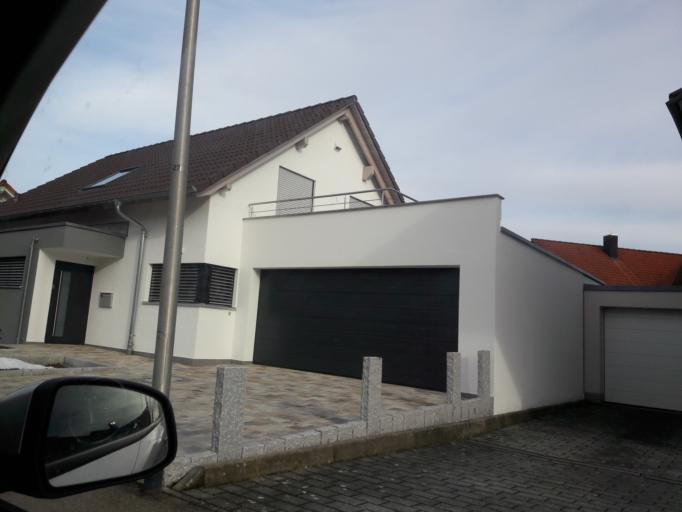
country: DE
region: Baden-Wuerttemberg
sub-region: Regierungsbezirk Stuttgart
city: Aspach
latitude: 48.9624
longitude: 9.4048
